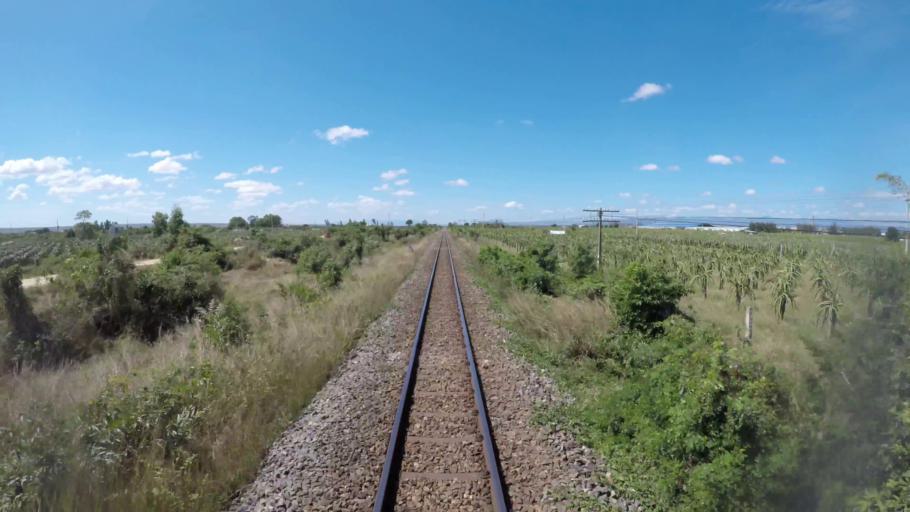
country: VN
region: Binh Thuan
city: Phan Thiet
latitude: 10.9853
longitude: 108.0171
